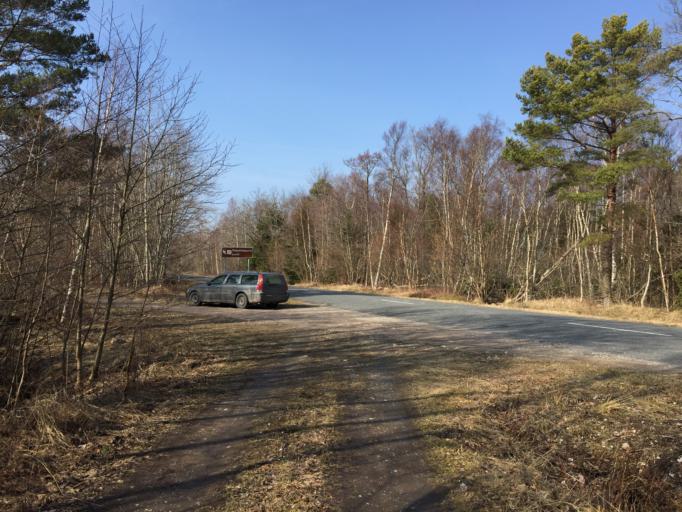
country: LV
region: Dundaga
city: Dundaga
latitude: 57.9309
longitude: 22.0253
